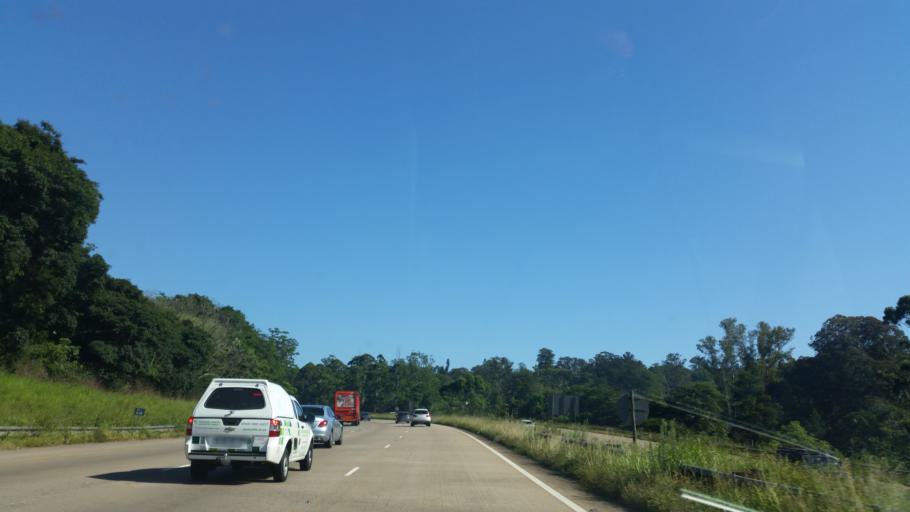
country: ZA
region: KwaZulu-Natal
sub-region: eThekwini Metropolitan Municipality
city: Mpumalanga
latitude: -29.7456
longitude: 30.6633
